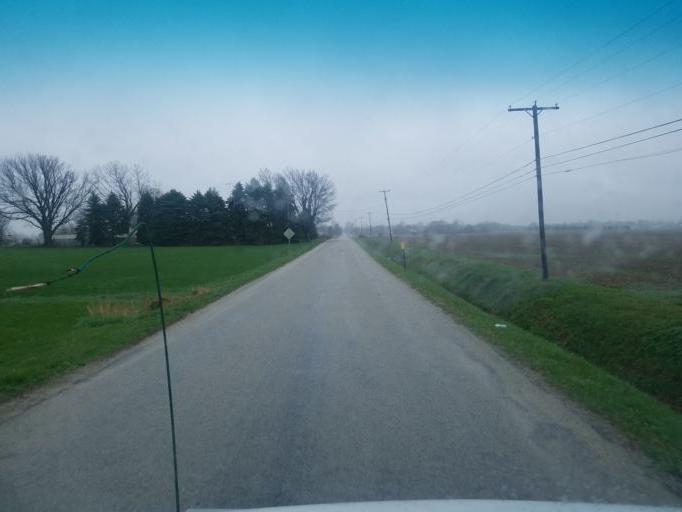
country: US
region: Ohio
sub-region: Wood County
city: North Baltimore
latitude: 41.2533
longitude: -83.6308
